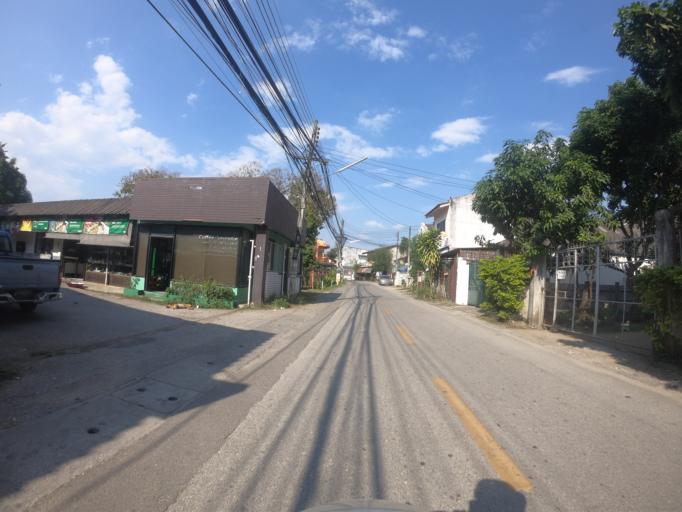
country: TH
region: Chiang Mai
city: Chiang Mai
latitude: 18.7875
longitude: 99.0226
